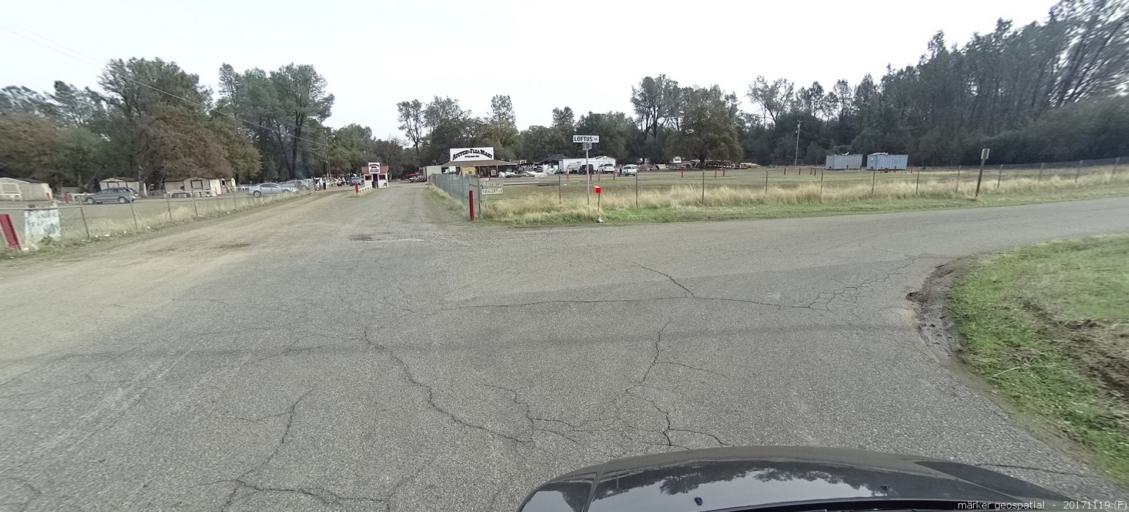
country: US
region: California
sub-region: Shasta County
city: Anderson
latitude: 40.4912
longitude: -122.2745
